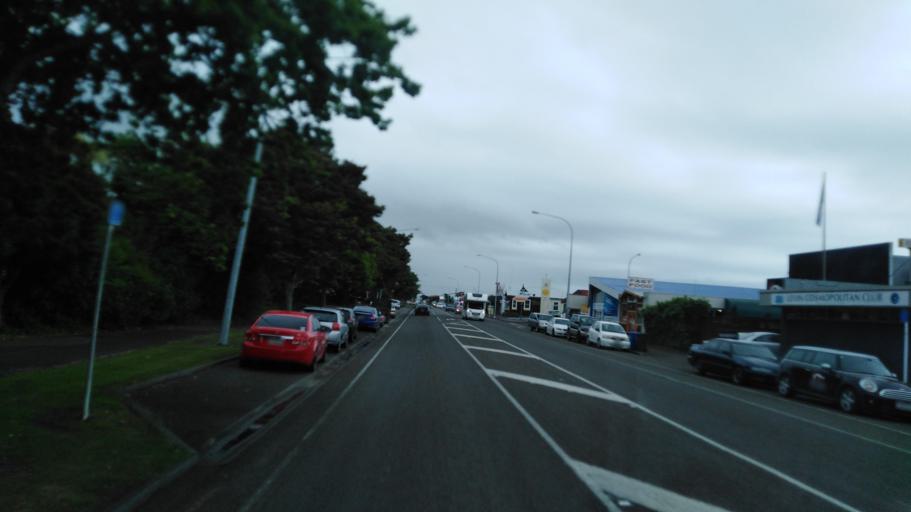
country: NZ
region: Manawatu-Wanganui
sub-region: Horowhenua District
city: Levin
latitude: -40.6304
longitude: 175.2785
